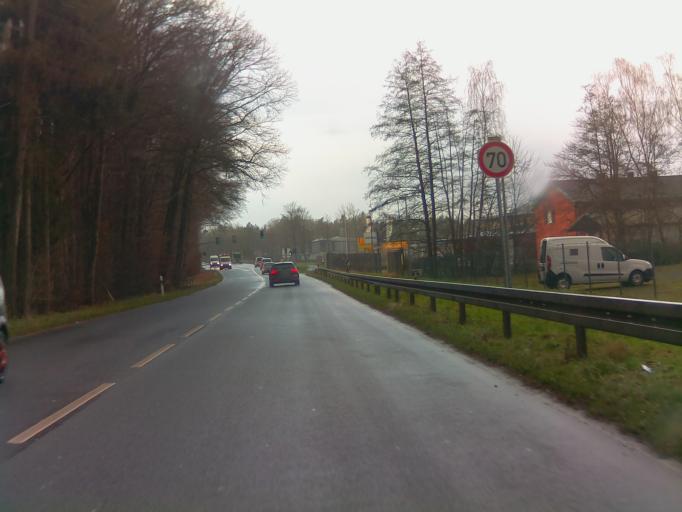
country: DE
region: Hesse
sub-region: Regierungsbezirk Darmstadt
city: Langenselbold
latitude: 50.1618
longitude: 9.0828
